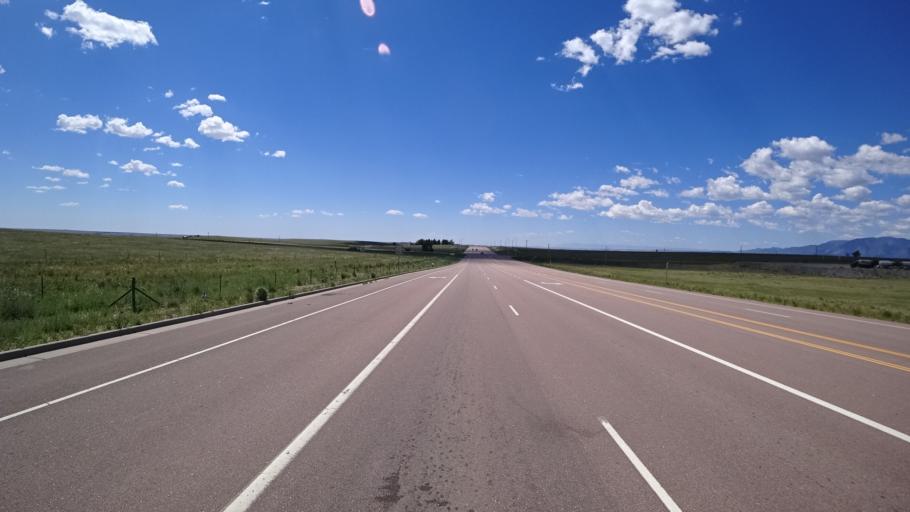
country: US
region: Colorado
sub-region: El Paso County
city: Cimarron Hills
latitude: 38.8406
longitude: -104.6828
